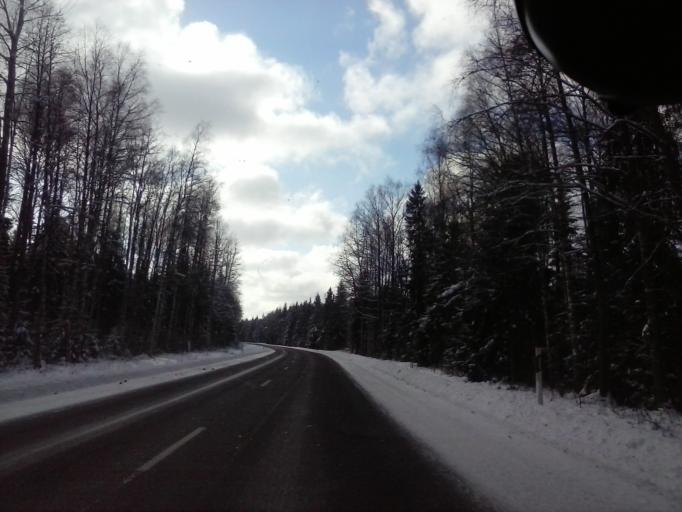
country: EE
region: Viljandimaa
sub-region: Moisakuela linn
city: Moisakula
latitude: 58.2394
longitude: 25.1240
